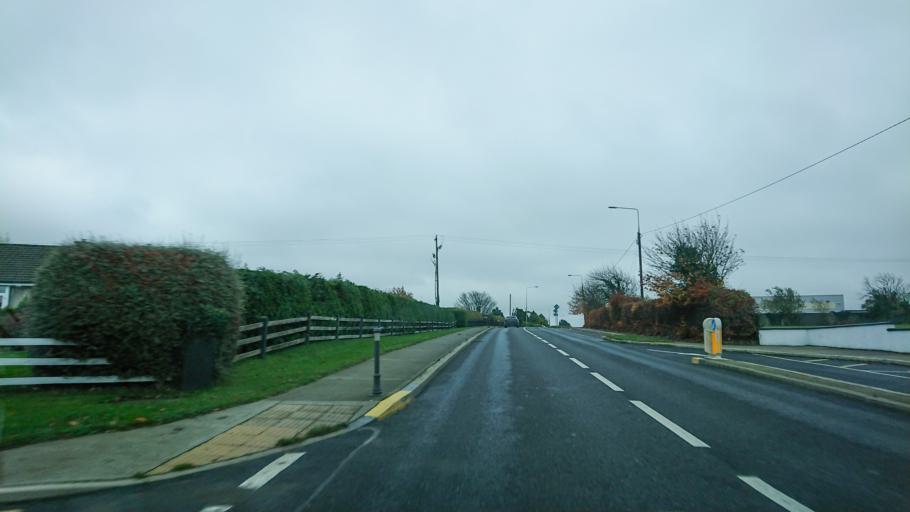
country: IE
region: Leinster
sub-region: Kilkenny
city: Mooncoin
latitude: 52.2912
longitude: -7.2496
